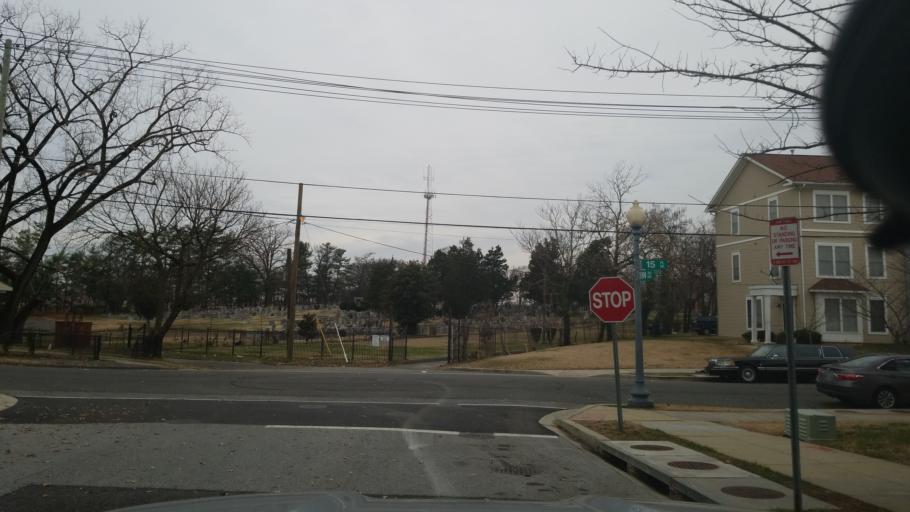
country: US
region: Maryland
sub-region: Prince George's County
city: Hillcrest Heights
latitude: 38.8484
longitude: -76.9824
